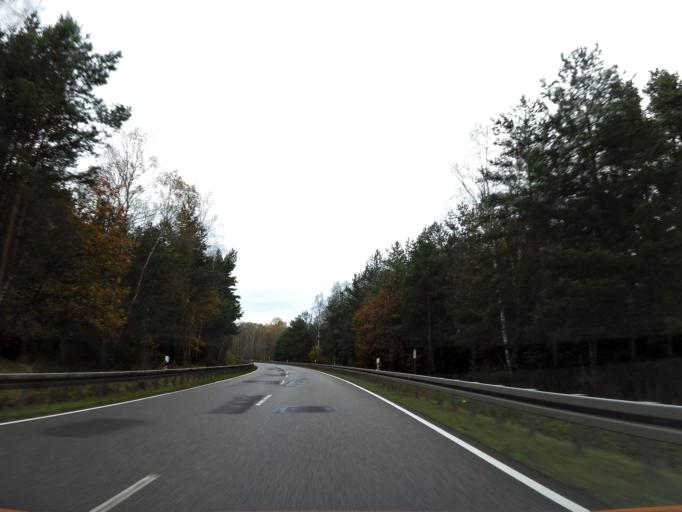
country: DE
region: Saxony-Anhalt
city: Colbitz
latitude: 52.3508
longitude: 11.5677
